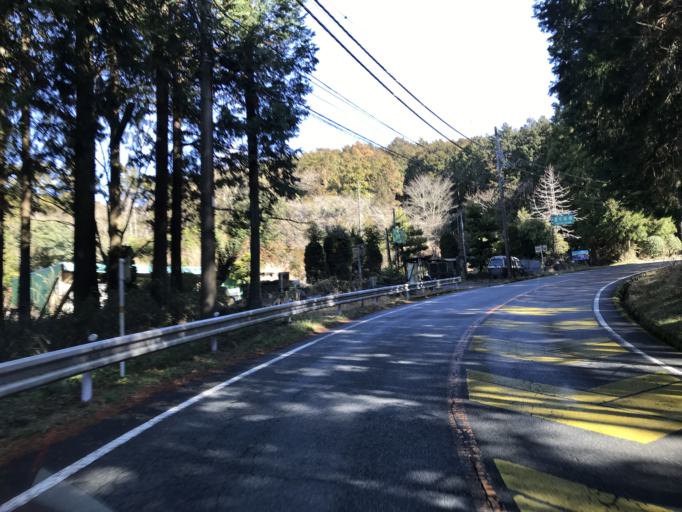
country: JP
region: Shizuoka
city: Fujinomiya
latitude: 35.2734
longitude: 138.6446
